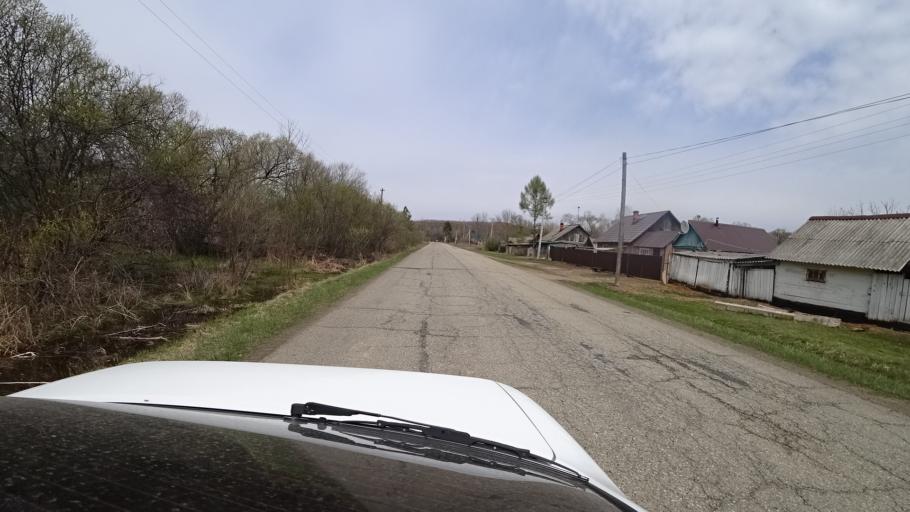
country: RU
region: Primorskiy
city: Novopokrovka
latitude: 45.7868
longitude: 134.1151
